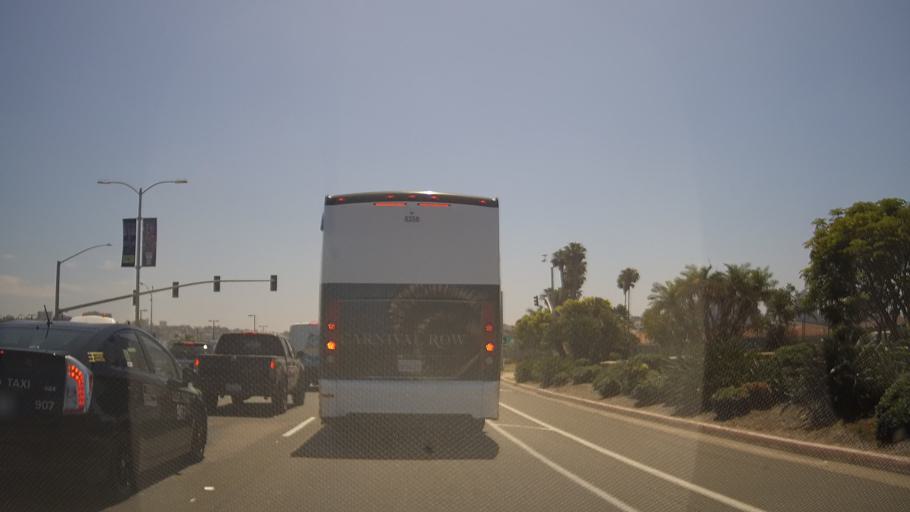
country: US
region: California
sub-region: San Diego County
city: San Diego
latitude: 32.7285
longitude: -117.1852
